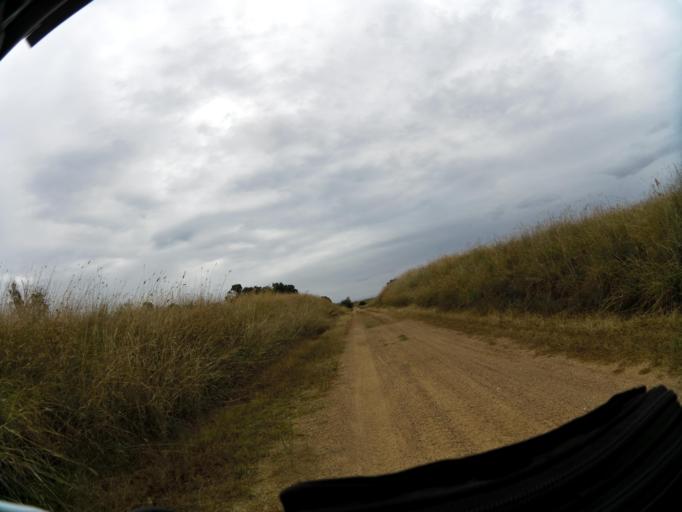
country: AU
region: New South Wales
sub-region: Albury Municipality
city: East Albury
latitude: -36.2064
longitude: 147.0521
